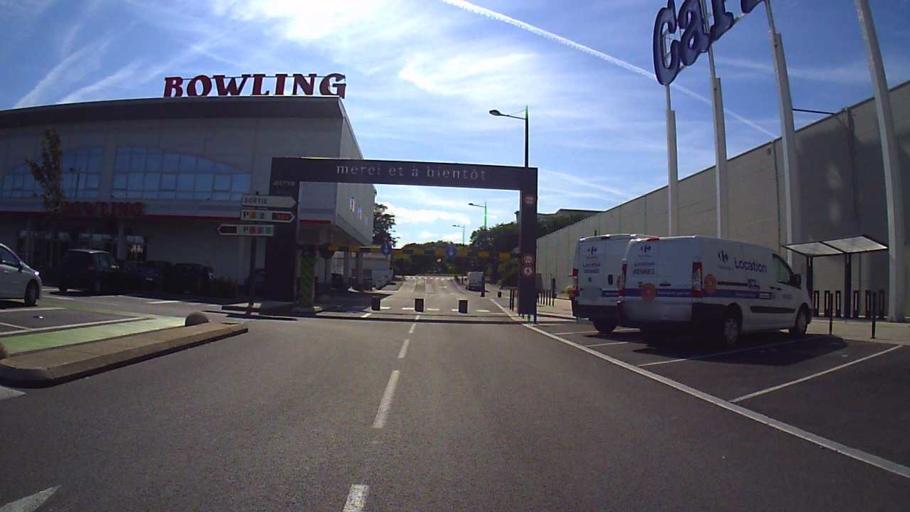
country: FR
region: Brittany
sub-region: Departement d'Ille-et-Vilaine
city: Rennes
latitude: 48.0823
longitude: -1.6805
